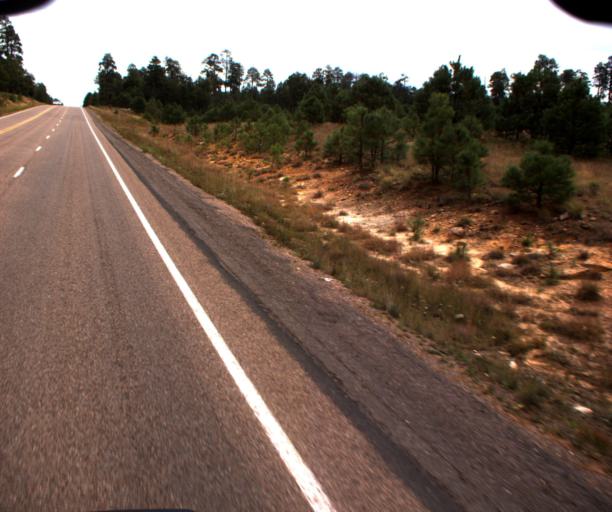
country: US
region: Arizona
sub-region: Navajo County
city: Heber-Overgaard
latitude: 34.3317
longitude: -110.7634
